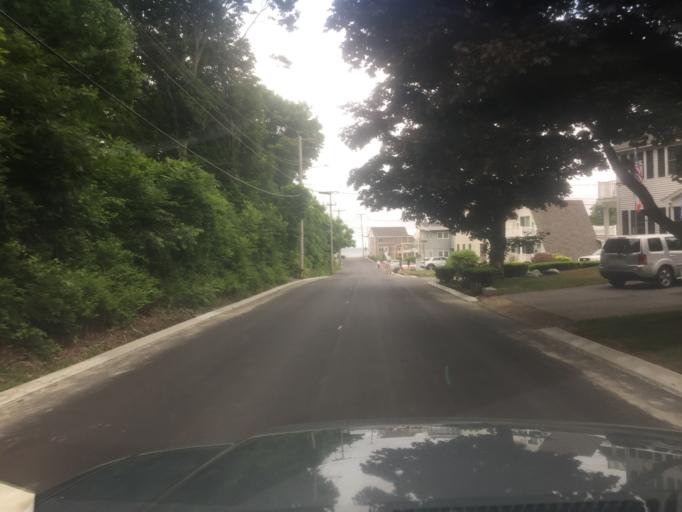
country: US
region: Maine
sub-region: York County
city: York Beach
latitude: 43.1569
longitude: -70.6247
